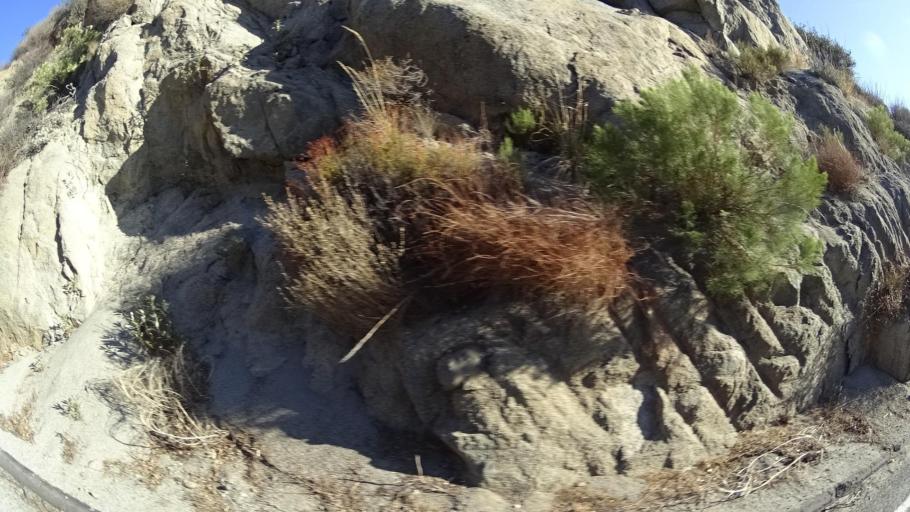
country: MX
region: Baja California
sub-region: Tecate
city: Hacienda Tecate
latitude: 32.5993
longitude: -116.5724
